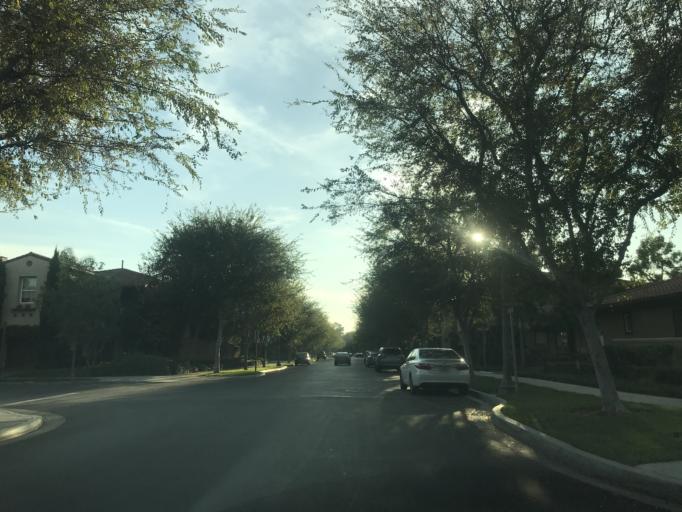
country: US
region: California
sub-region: Orange County
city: Irvine
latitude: 33.6999
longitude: -117.7606
